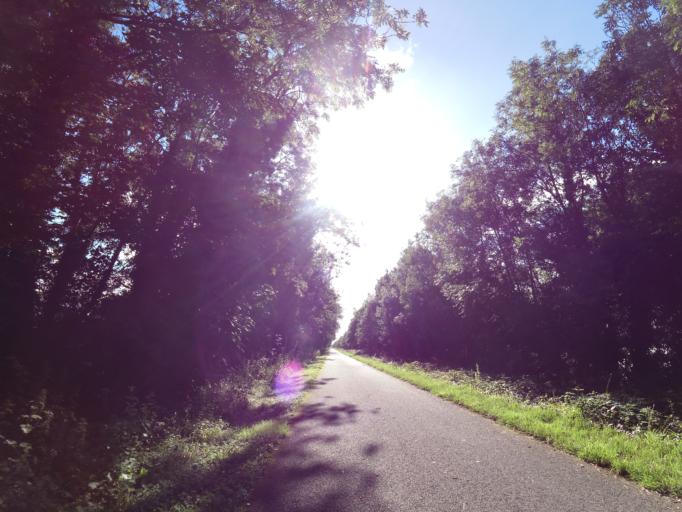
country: IE
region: Leinster
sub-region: An Iarmhi
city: Moate
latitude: 53.3999
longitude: -7.7140
